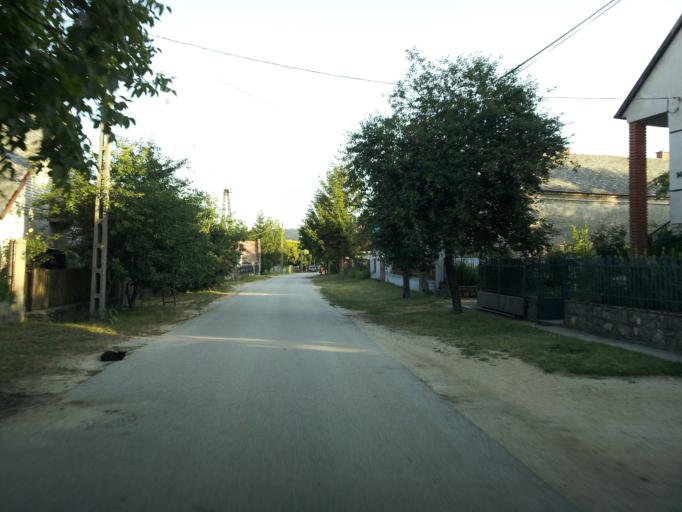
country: HU
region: Veszprem
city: Ajka
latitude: 46.9836
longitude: 17.5677
